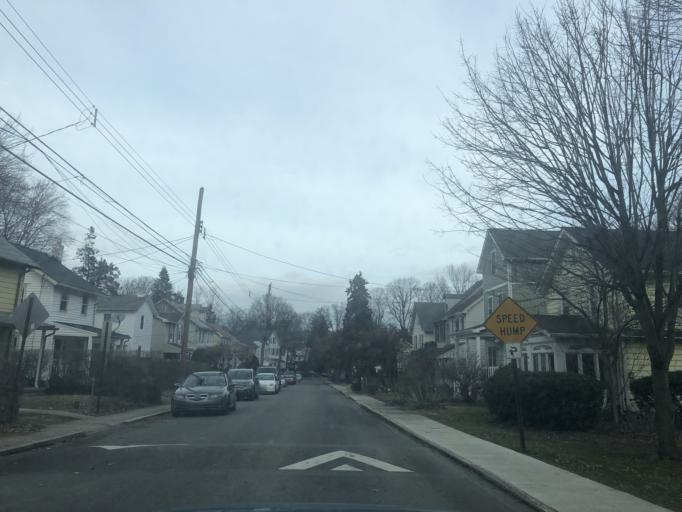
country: US
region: Pennsylvania
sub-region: Delaware County
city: Radnor
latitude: 40.0276
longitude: -75.3354
